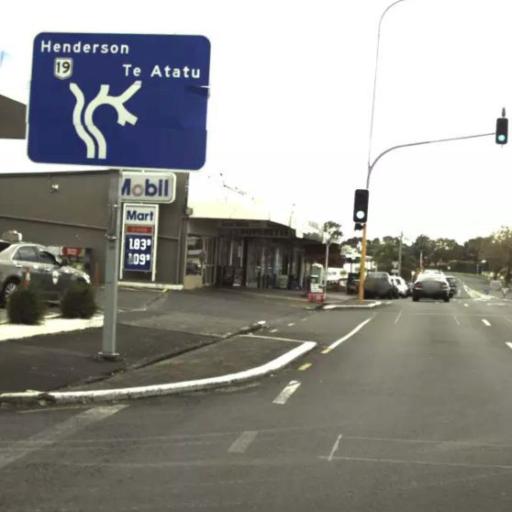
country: NZ
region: Auckland
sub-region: Auckland
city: Rosebank
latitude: -36.8870
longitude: 174.6443
